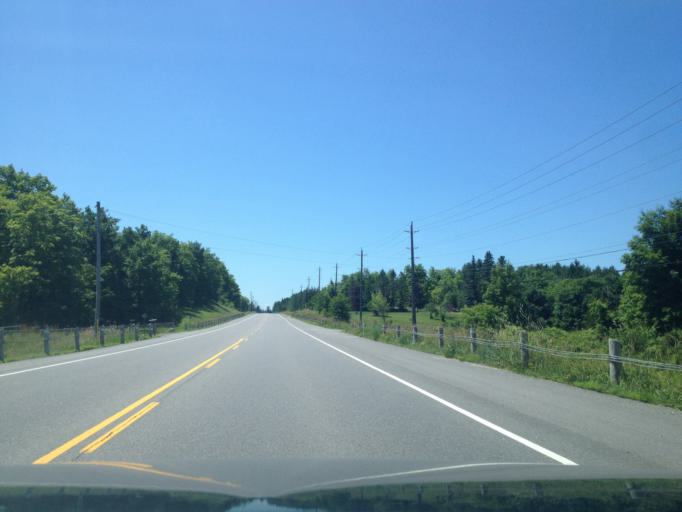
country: CA
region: Ontario
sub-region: Wellington County
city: Guelph
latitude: 43.6148
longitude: -80.1014
